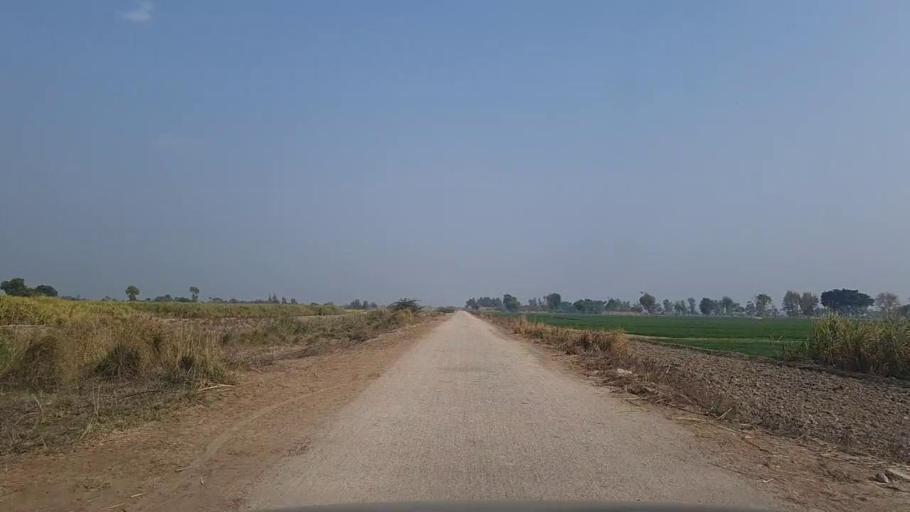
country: PK
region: Sindh
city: Nawabshah
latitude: 26.2770
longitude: 68.4327
